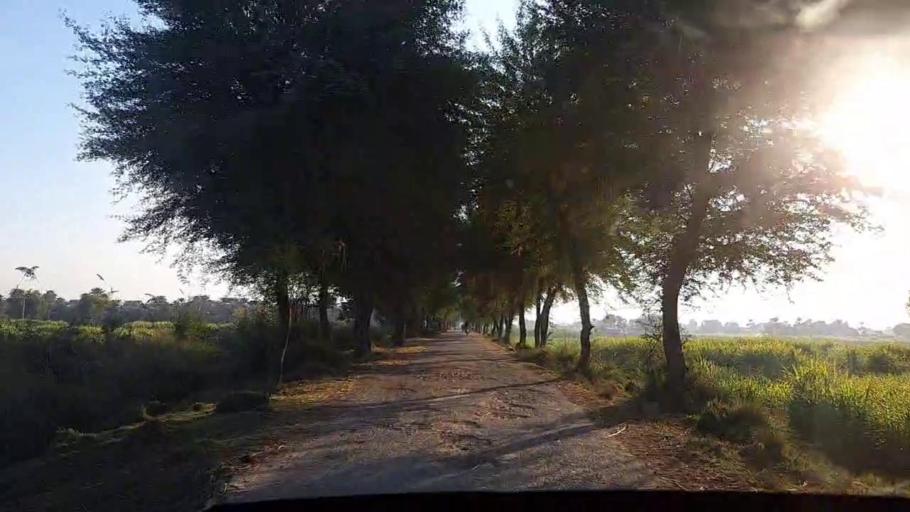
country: PK
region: Sindh
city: Sobhadero
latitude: 27.4058
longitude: 68.3919
